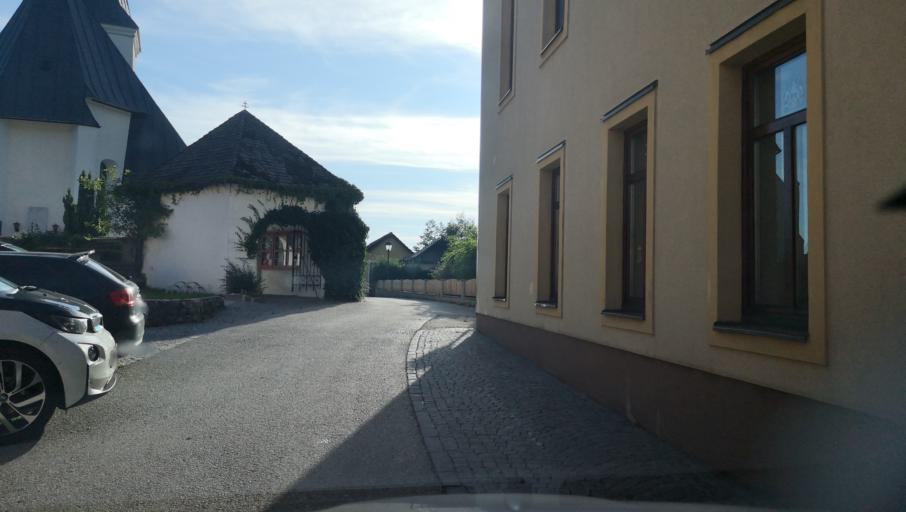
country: AT
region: Lower Austria
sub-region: Waidhofen an der Ybbs Stadt
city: Waidhofen an der Ybbs
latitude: 47.9797
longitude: 14.8026
